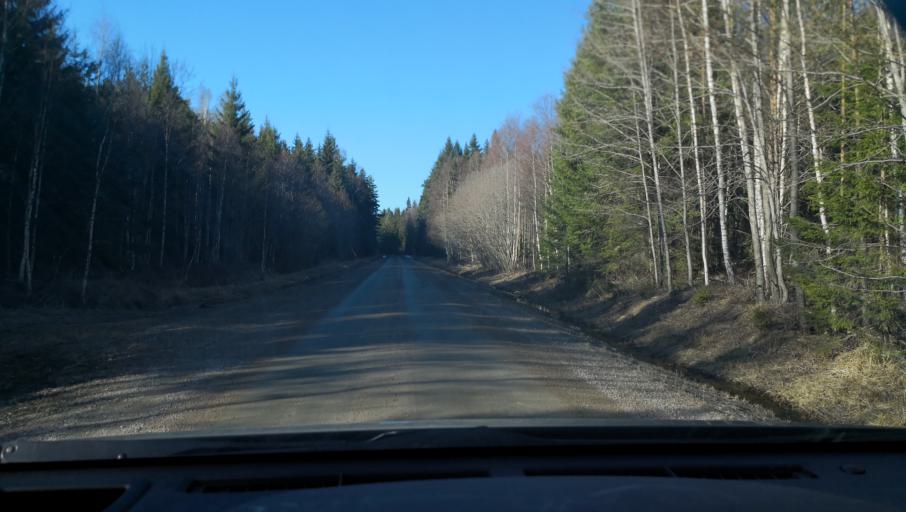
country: SE
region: Vaestmanland
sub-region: Sala Kommun
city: Sala
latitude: 60.1400
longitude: 16.6489
